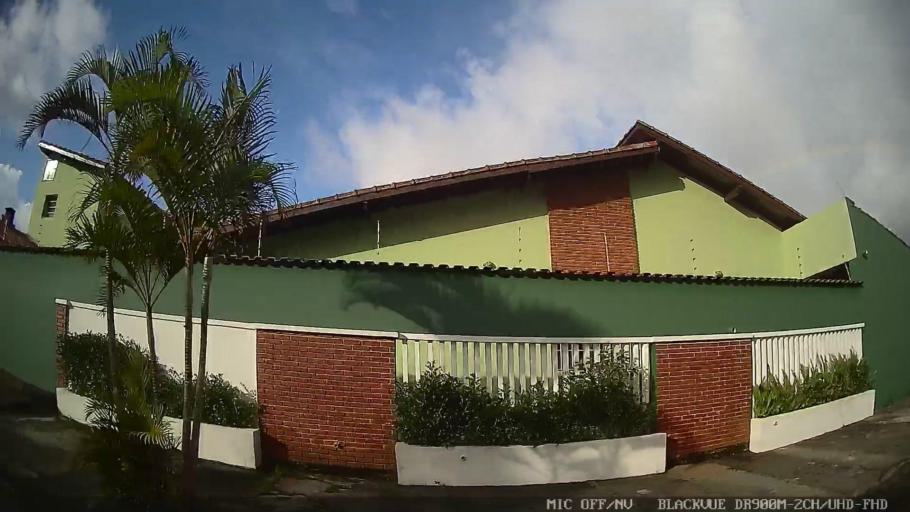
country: BR
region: Sao Paulo
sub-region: Itanhaem
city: Itanhaem
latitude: -24.2100
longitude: -46.8388
